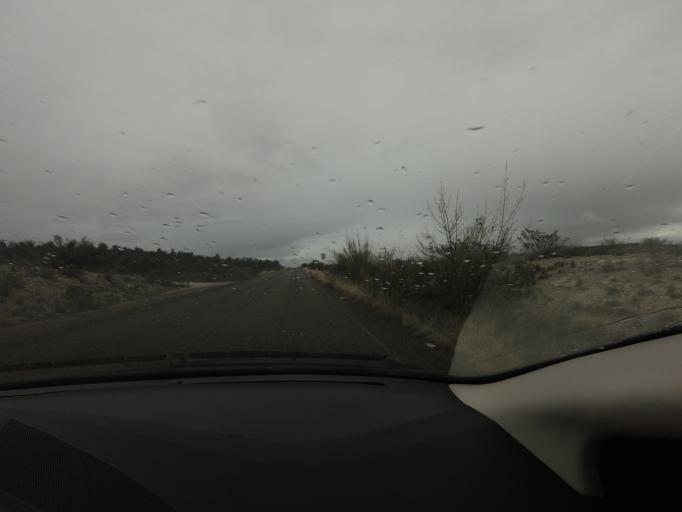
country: US
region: Arizona
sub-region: Yavapai County
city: Camp Verde
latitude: 34.6058
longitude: -111.8558
